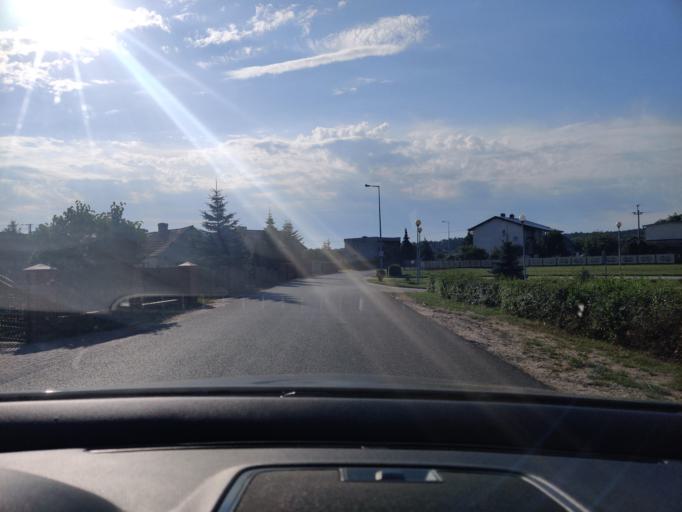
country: PL
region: Greater Poland Voivodeship
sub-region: Konin
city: Konin
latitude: 52.1891
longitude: 18.3215
